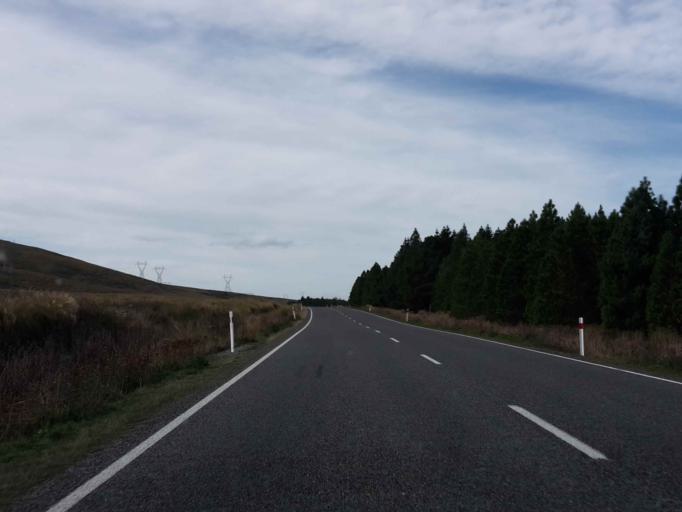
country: NZ
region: Canterbury
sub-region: Timaru District
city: Pleasant Point
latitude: -44.0907
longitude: 170.5879
